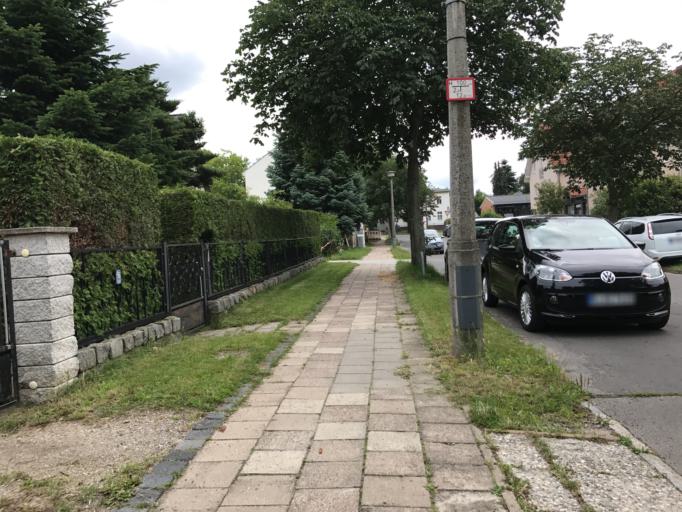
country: DE
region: Berlin
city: Karow
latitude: 52.6119
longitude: 13.4817
